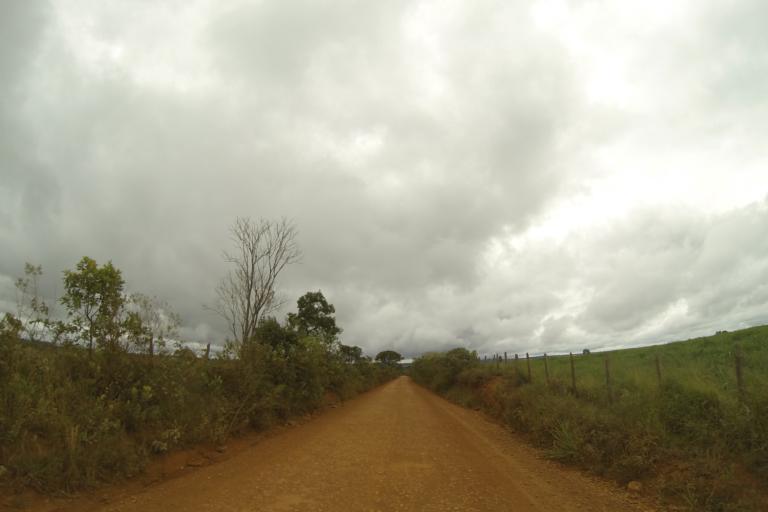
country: BR
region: Minas Gerais
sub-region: Campos Altos
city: Campos Altos
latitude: -19.7885
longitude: -46.3685
